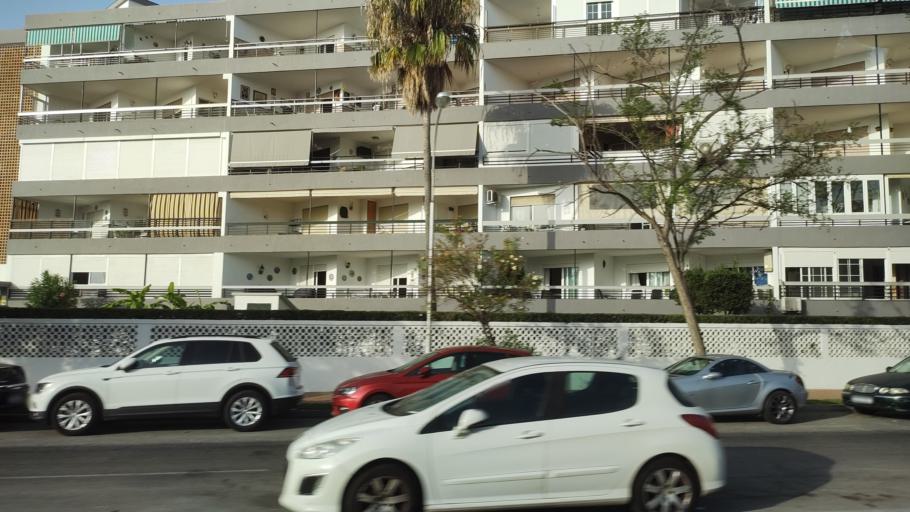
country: ES
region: Andalusia
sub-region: Provincia de Malaga
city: Torremolinos
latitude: 36.6432
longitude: -4.4827
